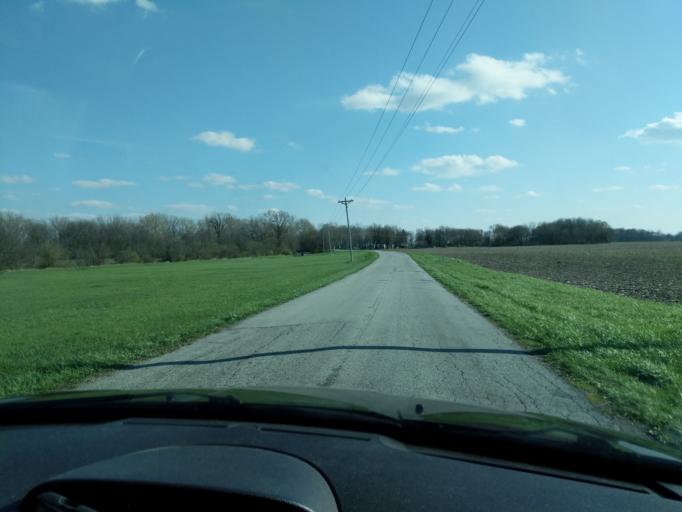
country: US
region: Ohio
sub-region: Champaign County
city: Urbana
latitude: 40.1366
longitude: -83.8109
